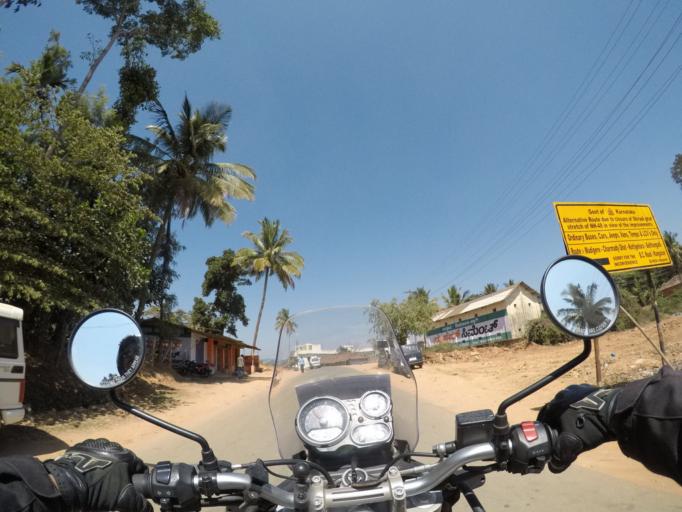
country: IN
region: Karnataka
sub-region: Chikmagalur
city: Mudigere
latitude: 13.0805
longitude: 75.6829
